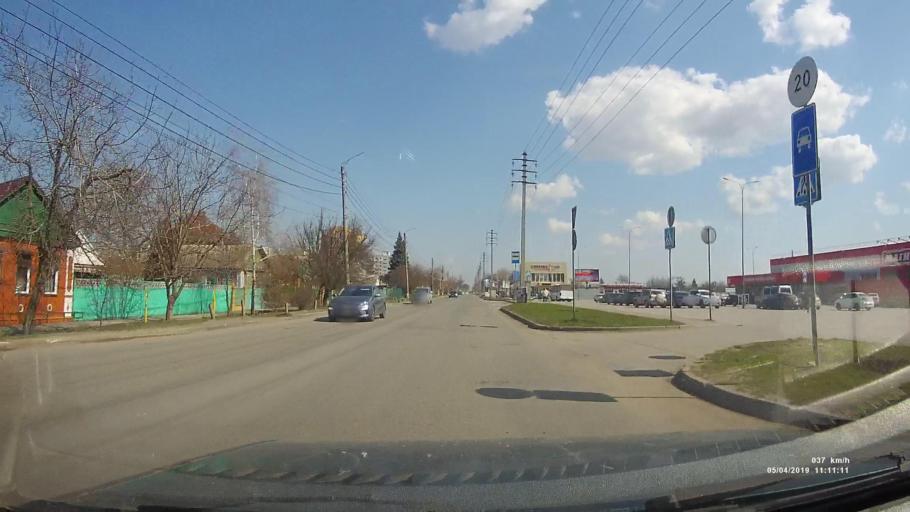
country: RU
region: Rostov
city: Azov
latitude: 47.0938
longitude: 39.4332
